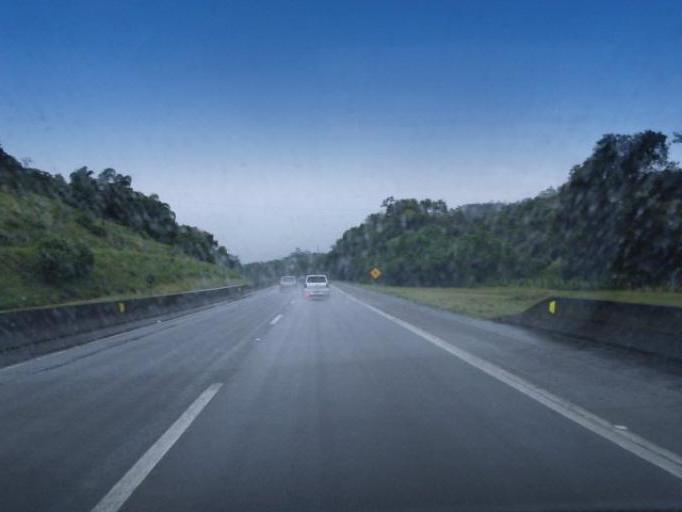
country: BR
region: Santa Catarina
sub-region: Joinville
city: Joinville
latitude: -26.4307
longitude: -48.8236
